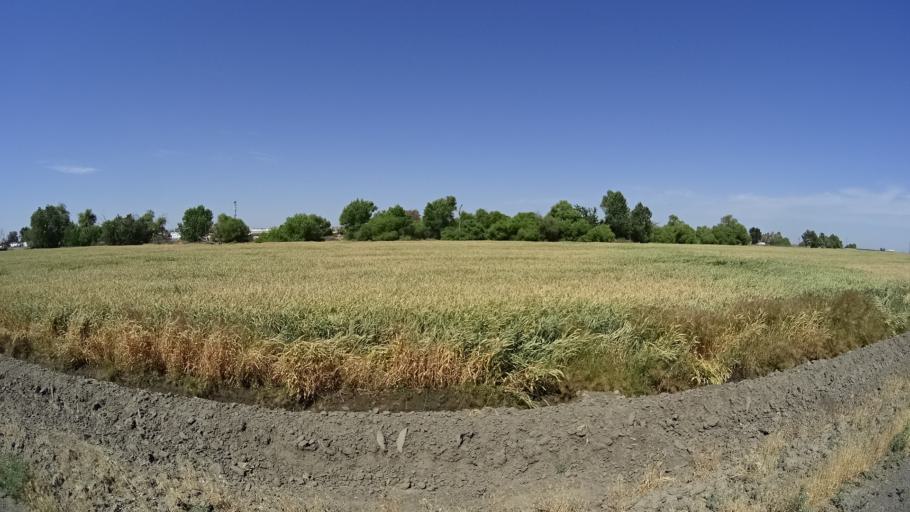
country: US
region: California
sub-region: Kings County
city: Stratford
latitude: 36.1933
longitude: -119.8159
